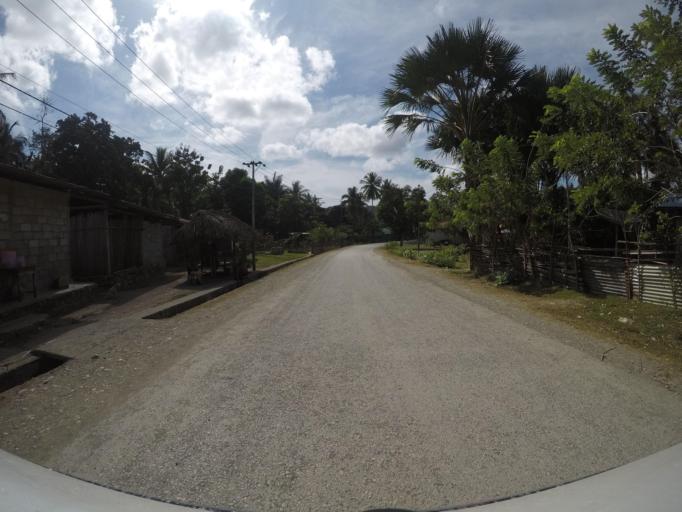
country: TL
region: Viqueque
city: Viqueque
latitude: -8.8542
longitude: 126.3610
